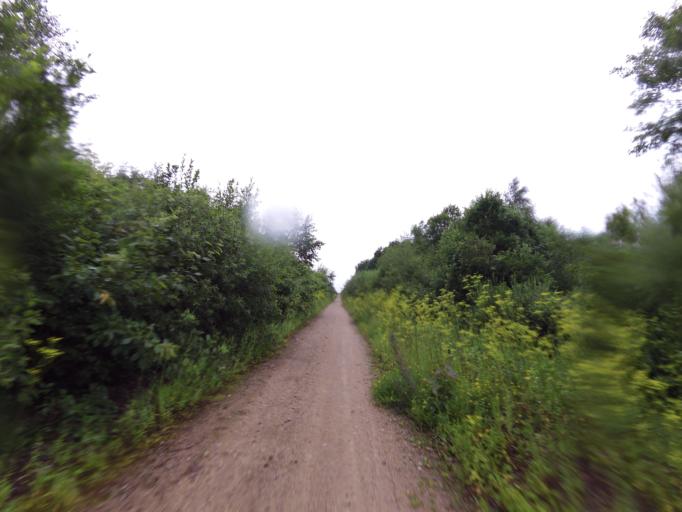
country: EE
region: Laeaene
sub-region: Lihula vald
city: Lihula
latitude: 58.9579
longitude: 23.8724
